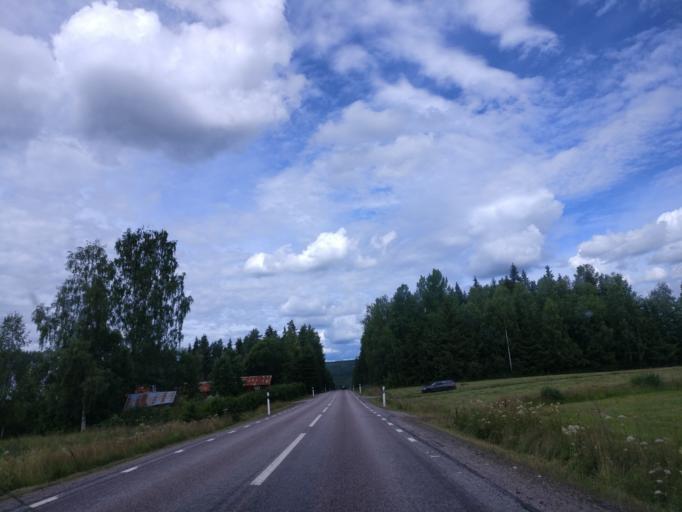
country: SE
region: Vaermland
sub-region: Hagfors Kommun
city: Ekshaerad
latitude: 60.1647
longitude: 13.4129
